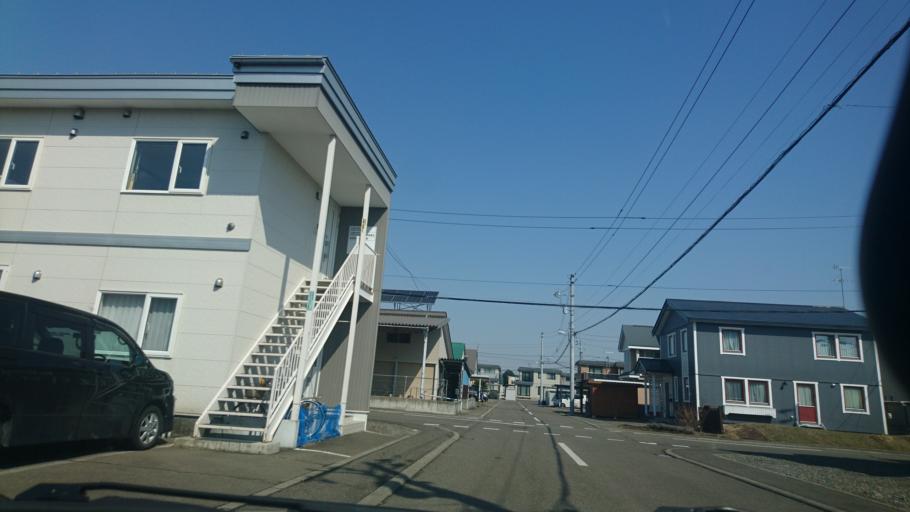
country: JP
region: Hokkaido
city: Obihiro
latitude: 42.9109
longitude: 143.0709
